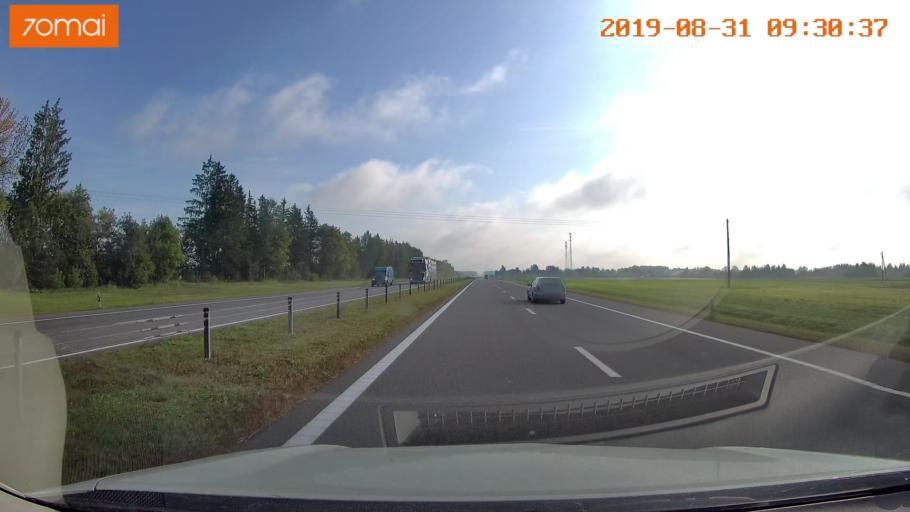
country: BY
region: Minsk
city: Byerazino
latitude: 53.8560
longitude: 29.1318
